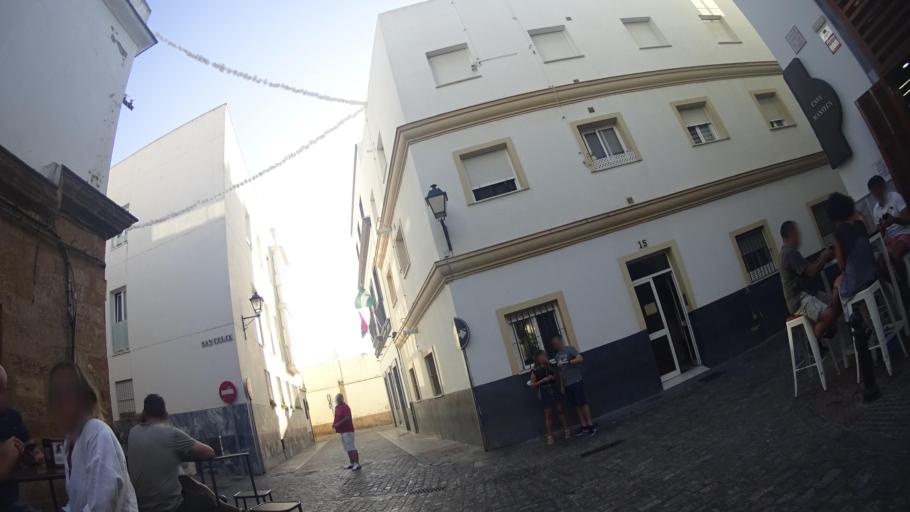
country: ES
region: Andalusia
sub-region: Provincia de Cadiz
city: Cadiz
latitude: 36.5301
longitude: -6.3036
